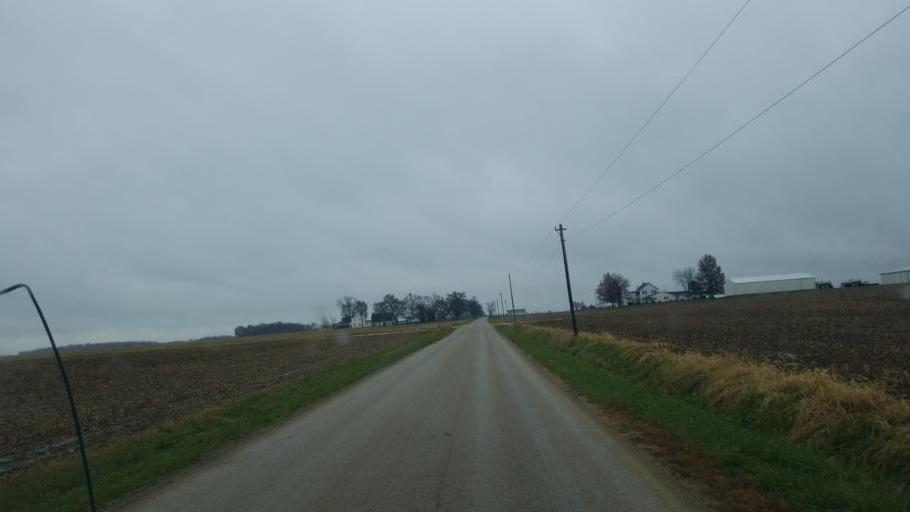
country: US
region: Indiana
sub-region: Adams County
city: Berne
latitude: 40.6741
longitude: -84.9172
